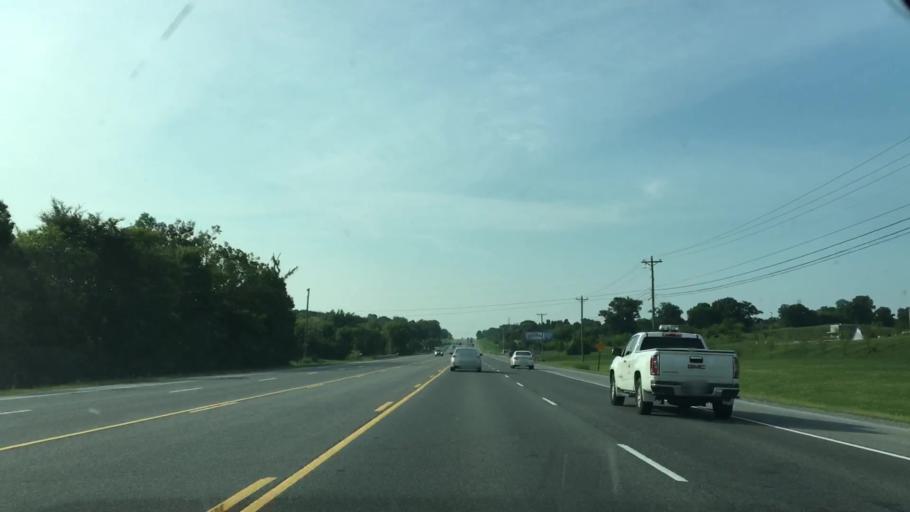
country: US
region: Tennessee
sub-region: Wilson County
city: Mount Juliet
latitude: 36.2213
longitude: -86.4247
